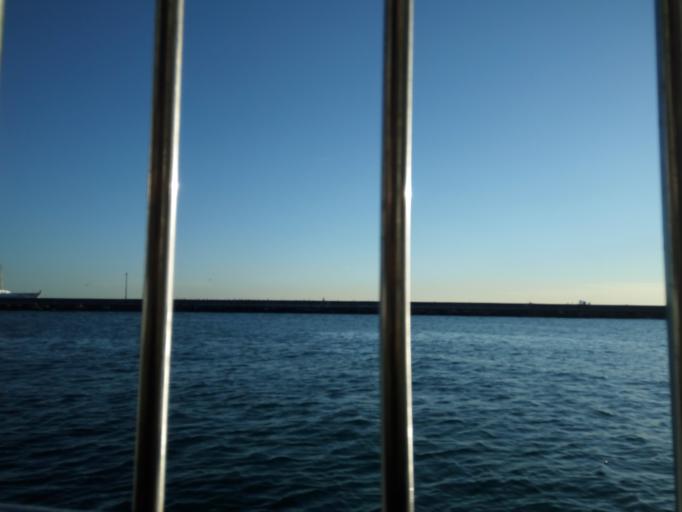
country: TR
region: Istanbul
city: UEskuedar
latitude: 40.9994
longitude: 29.0103
